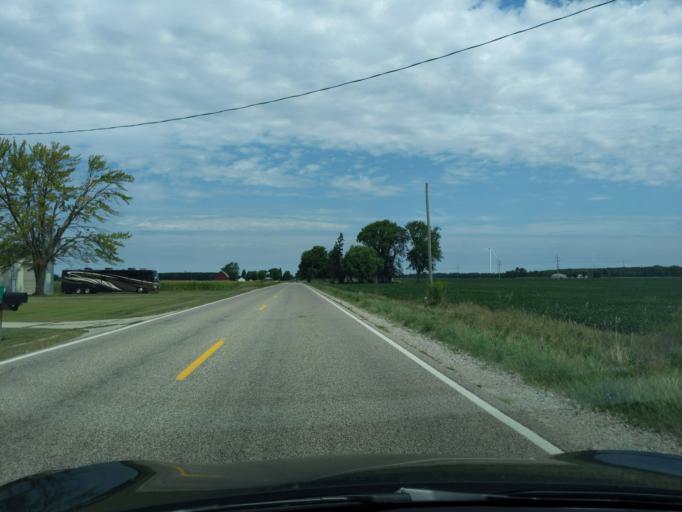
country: US
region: Michigan
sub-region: Gratiot County
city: Breckenridge
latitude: 43.3865
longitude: -84.4293
